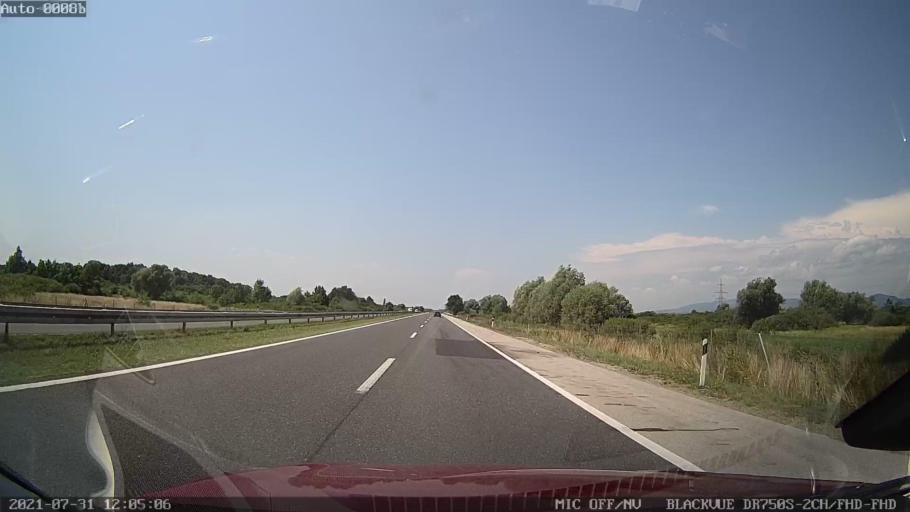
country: HR
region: Zagrebacka
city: Brckovljani
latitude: 45.8821
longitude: 16.2206
